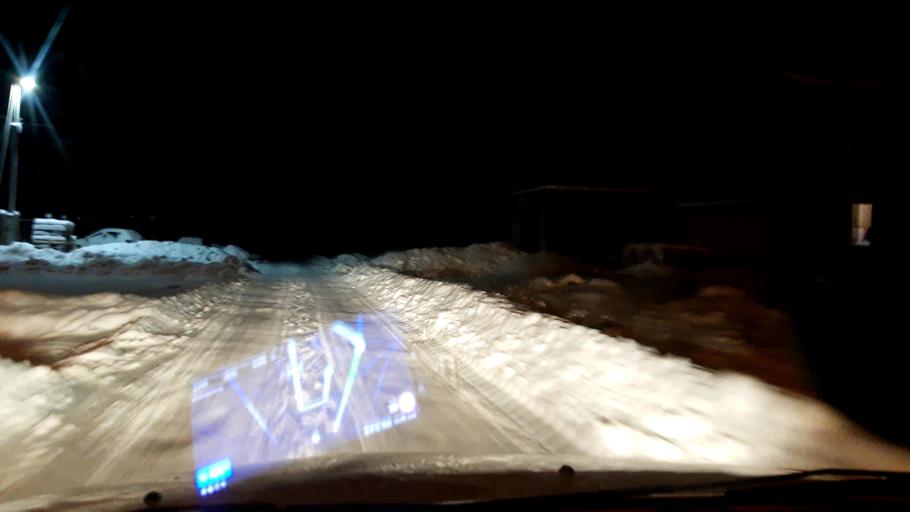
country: RU
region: Bashkortostan
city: Kabakovo
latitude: 54.6771
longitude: 56.1020
